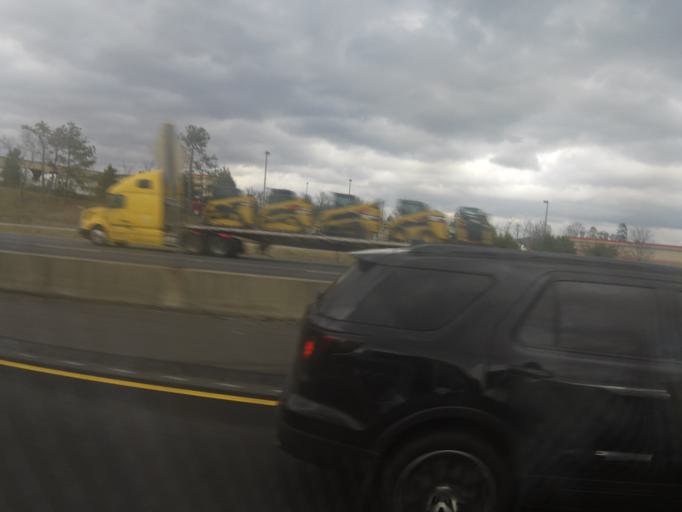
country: US
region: Georgia
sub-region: Catoosa County
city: Indian Springs
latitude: 34.9299
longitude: -85.1533
